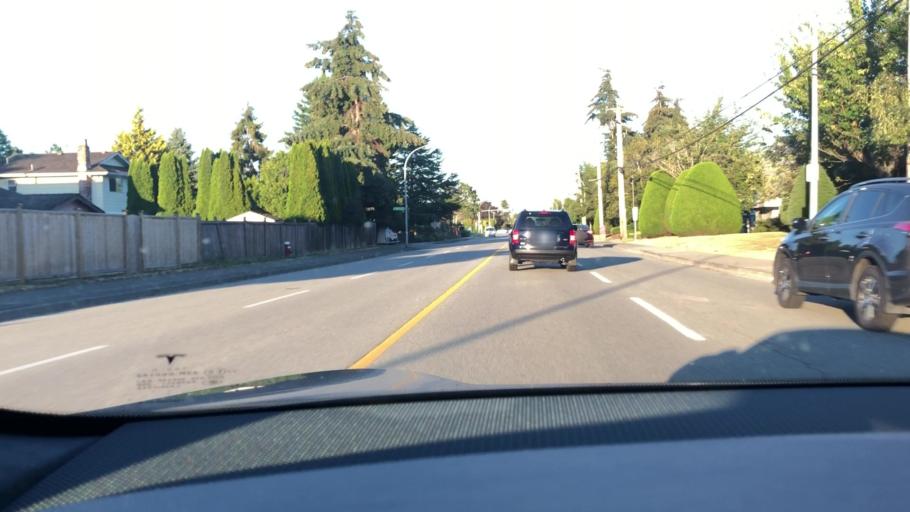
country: CA
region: British Columbia
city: Richmond
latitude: 49.1484
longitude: -123.1735
